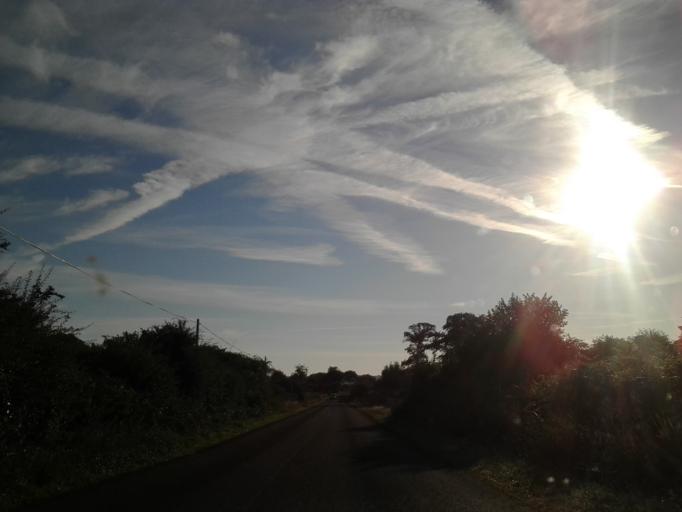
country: FR
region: Lower Normandy
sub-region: Departement de la Manche
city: Digosville
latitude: 49.6112
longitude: -1.4643
